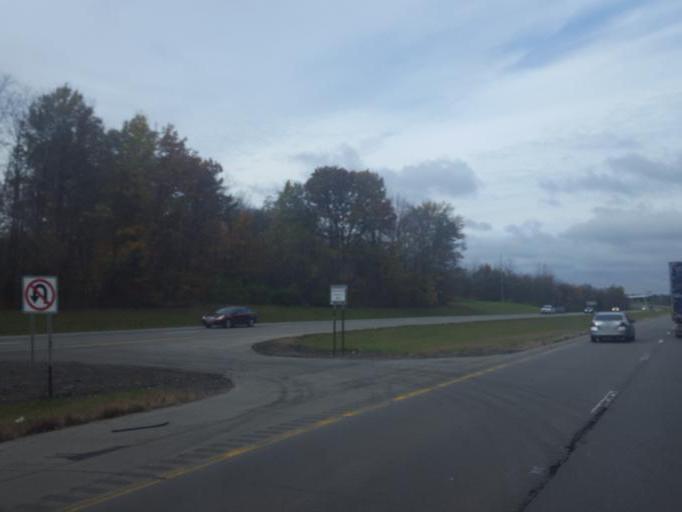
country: US
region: Ohio
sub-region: Richland County
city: Ontario
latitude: 40.7775
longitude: -82.5735
